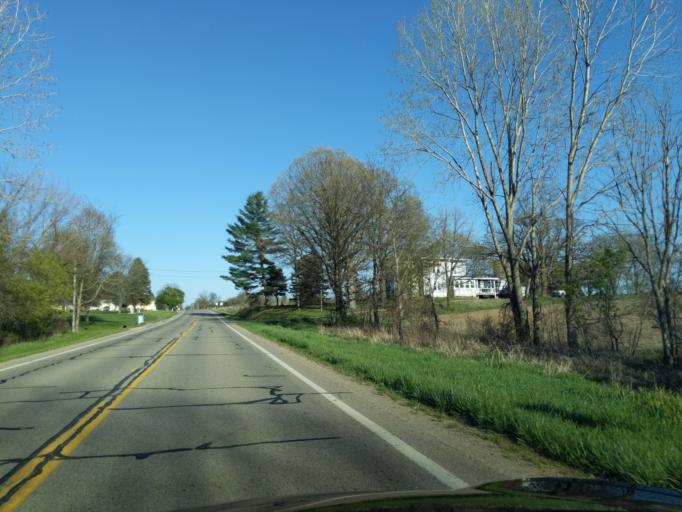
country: US
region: Michigan
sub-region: Eaton County
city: Grand Ledge
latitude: 42.8098
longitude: -84.7992
